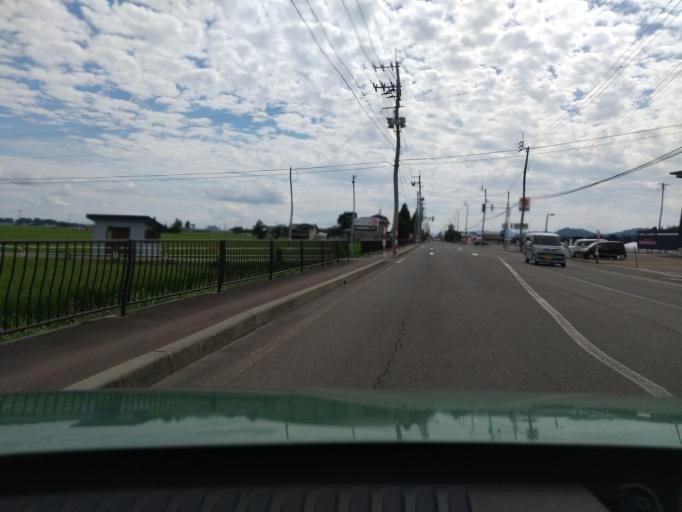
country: JP
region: Akita
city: Kakunodatemachi
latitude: 39.5580
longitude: 140.5554
